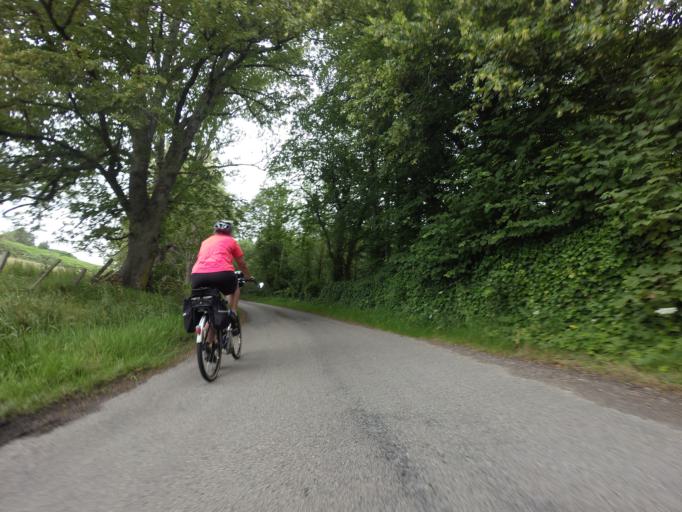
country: GB
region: Scotland
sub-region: Highland
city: Alness
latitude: 57.8925
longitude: -4.3747
